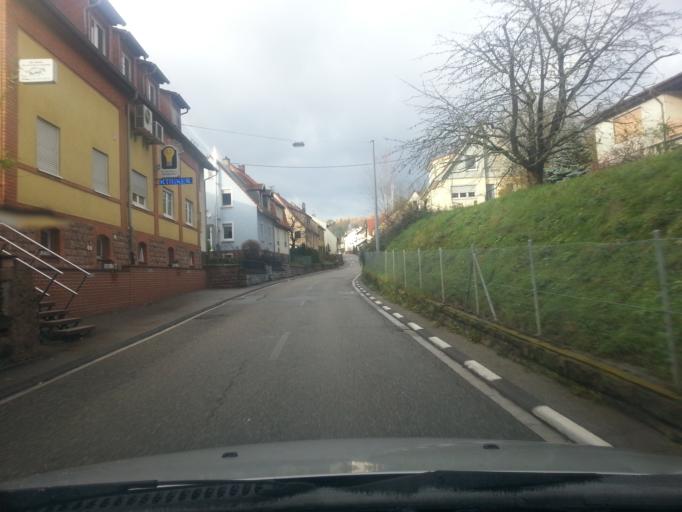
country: DE
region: Baden-Wuerttemberg
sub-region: Karlsruhe Region
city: Gaiberg
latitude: 49.3431
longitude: 8.7540
